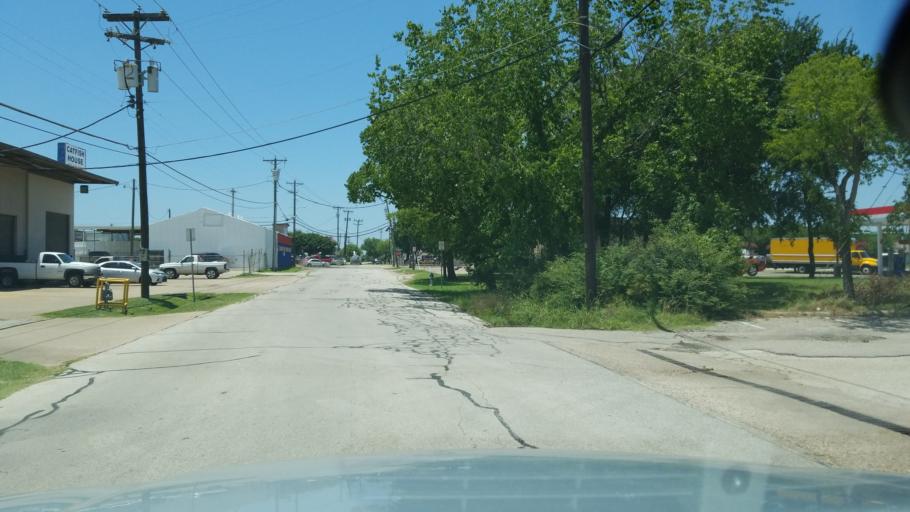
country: US
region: Texas
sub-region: Dallas County
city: Irving
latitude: 32.8085
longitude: -96.9244
